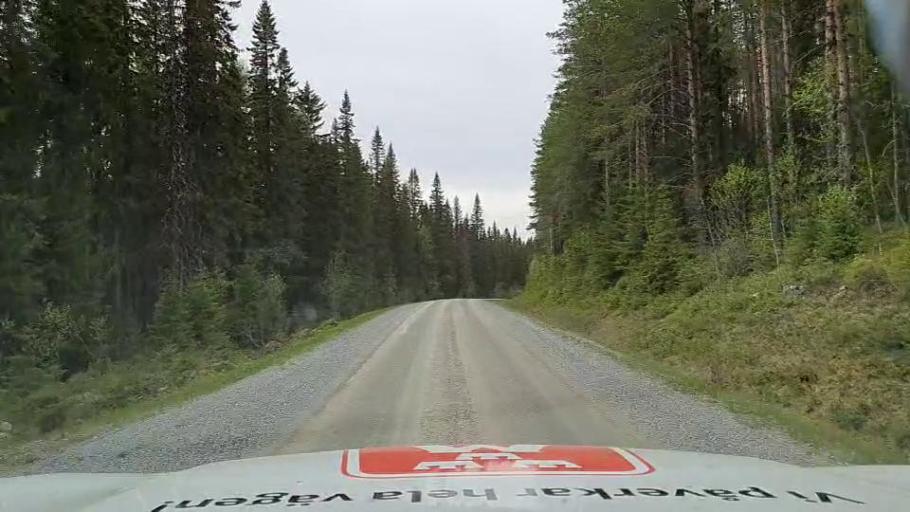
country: SE
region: Jaemtland
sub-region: OEstersunds Kommun
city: Brunflo
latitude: 62.6355
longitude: 14.9366
